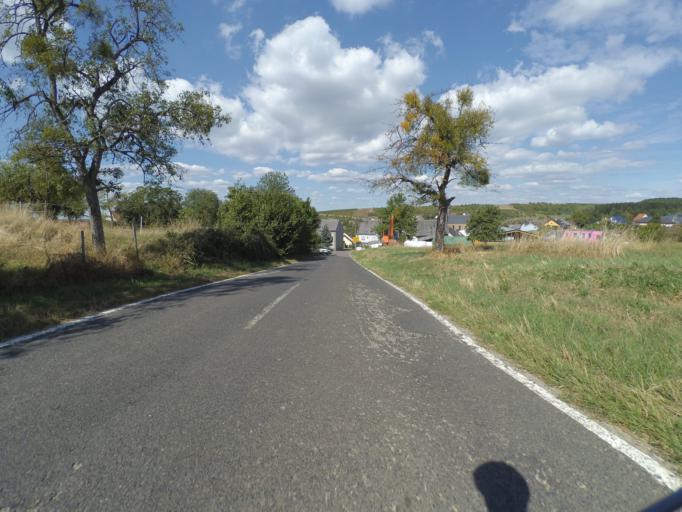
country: LU
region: Grevenmacher
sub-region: Canton de Grevenmacher
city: Wormeldange
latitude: 49.5856
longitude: 6.4157
